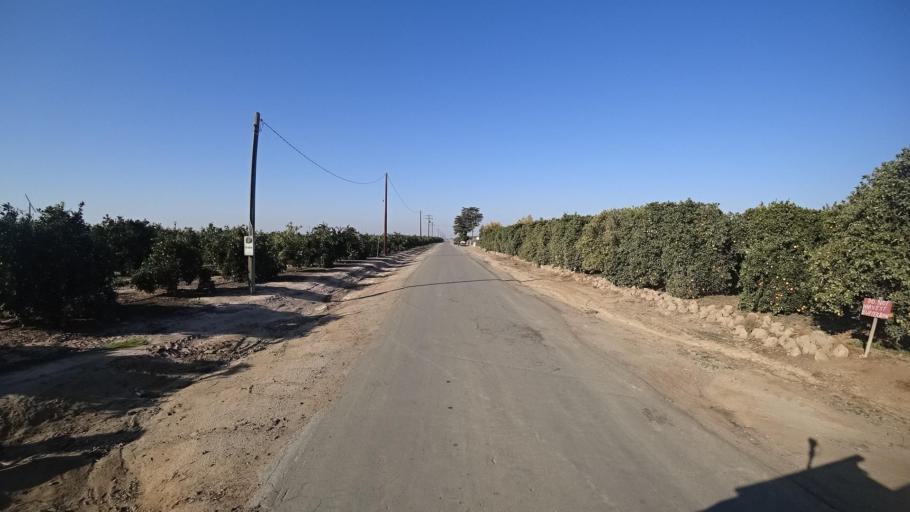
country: US
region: California
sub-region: Tulare County
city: Richgrove
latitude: 35.7253
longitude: -119.1407
